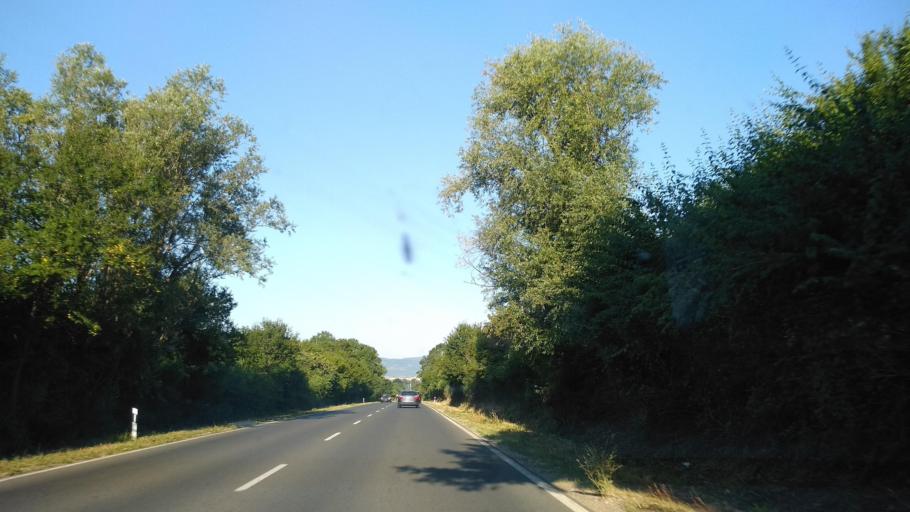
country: BG
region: Gabrovo
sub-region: Obshtina Sevlievo
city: Sevlievo
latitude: 43.0371
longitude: 25.1502
